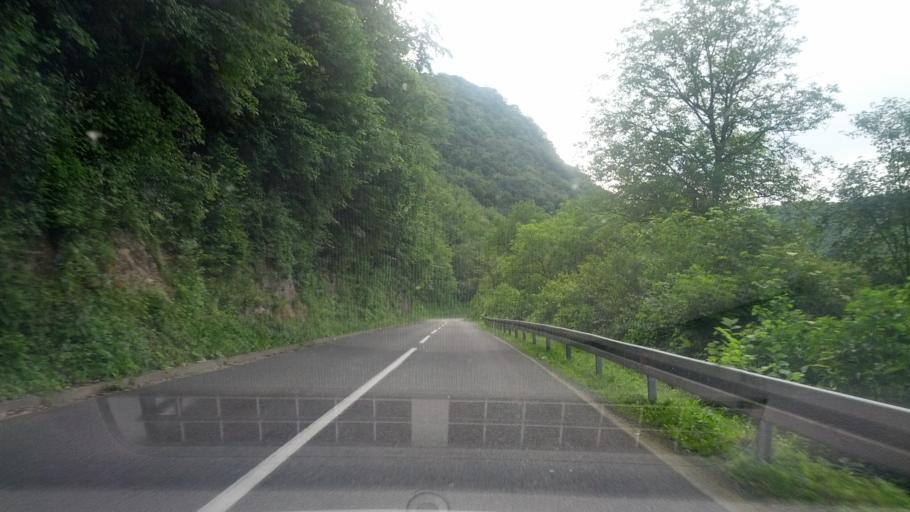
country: BA
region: Federation of Bosnia and Herzegovina
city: Ostrozac
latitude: 44.9085
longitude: 15.9812
